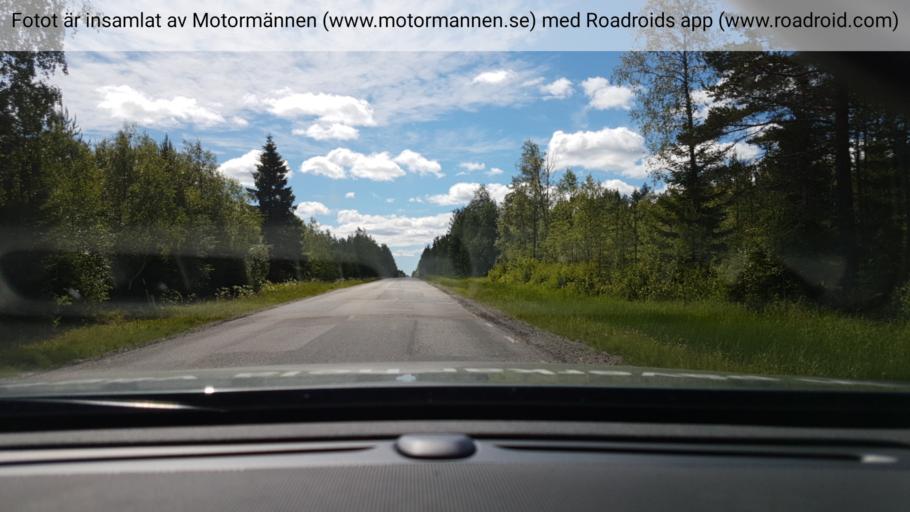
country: SE
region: Vaesterbotten
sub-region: Skelleftea Kommun
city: Burea
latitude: 64.4366
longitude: 21.3541
